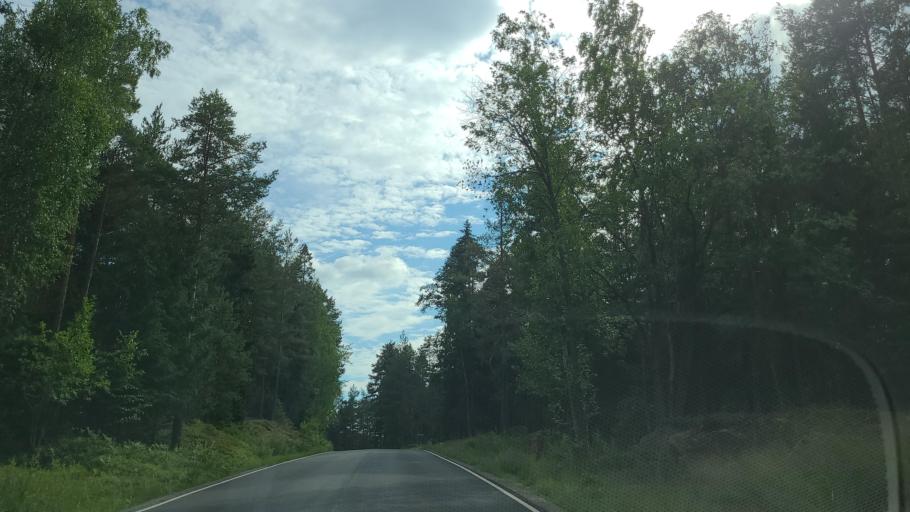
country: FI
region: Varsinais-Suomi
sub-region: Turku
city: Rymaettylae
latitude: 60.3245
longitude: 21.9572
